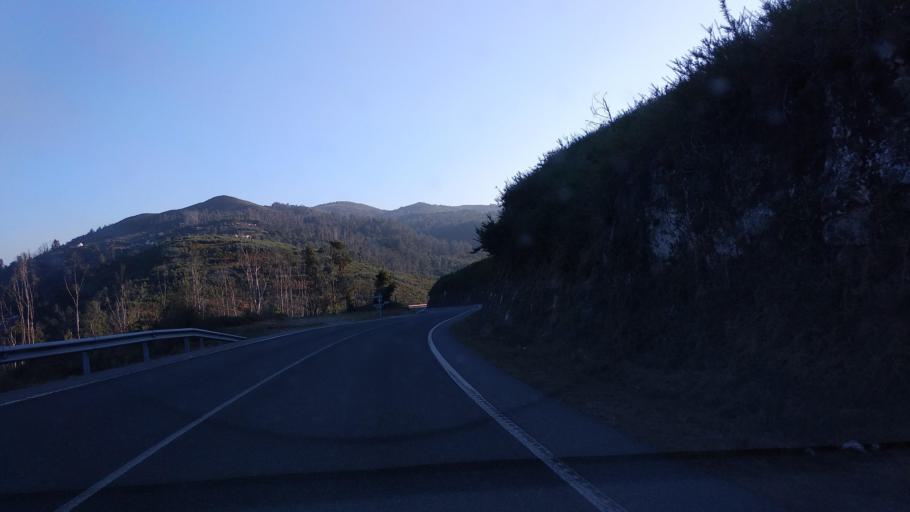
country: ES
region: Galicia
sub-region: Provincia de Pontevedra
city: Ponte Caldelas
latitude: 42.3435
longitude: -8.5429
